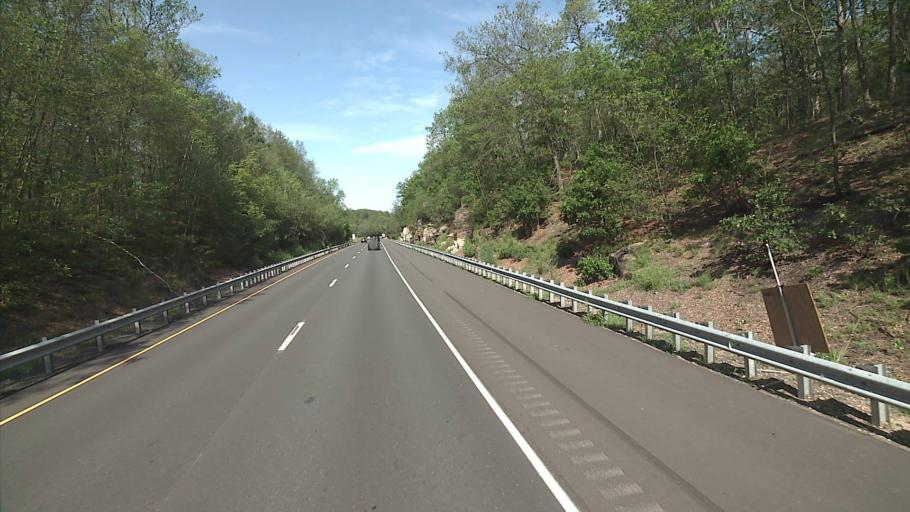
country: US
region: Connecticut
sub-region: Hartford County
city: Terramuggus
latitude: 41.6591
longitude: -72.5109
